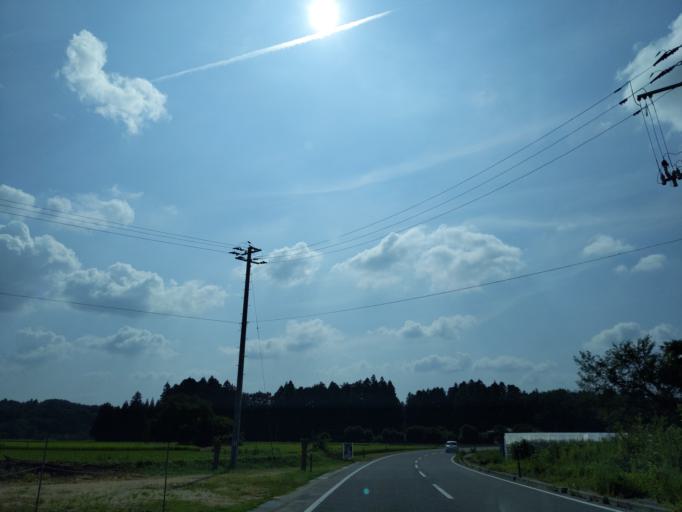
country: JP
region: Fukushima
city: Sukagawa
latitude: 37.3087
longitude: 140.3179
